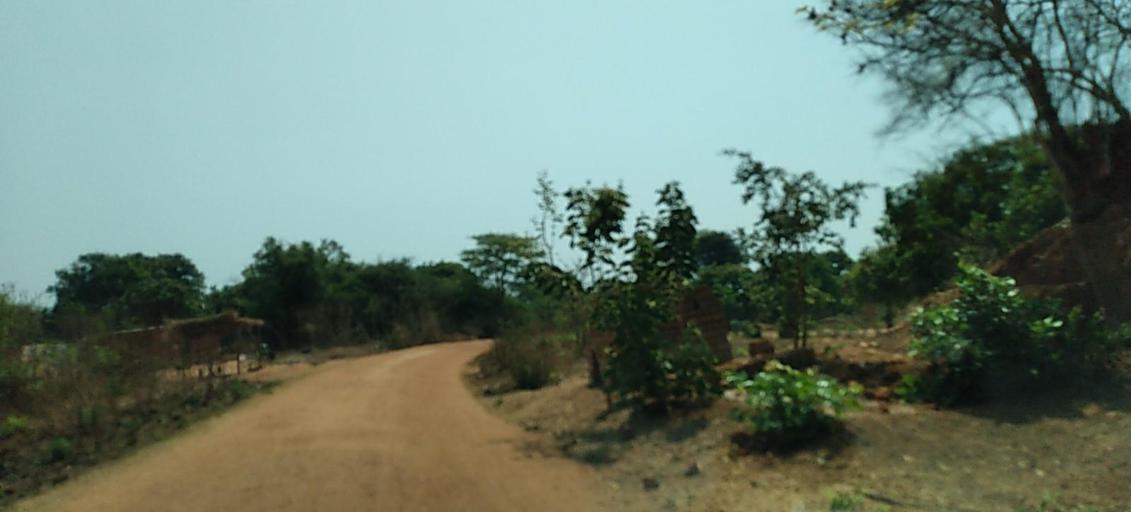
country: ZM
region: Copperbelt
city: Luanshya
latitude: -13.3491
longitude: 28.4019
